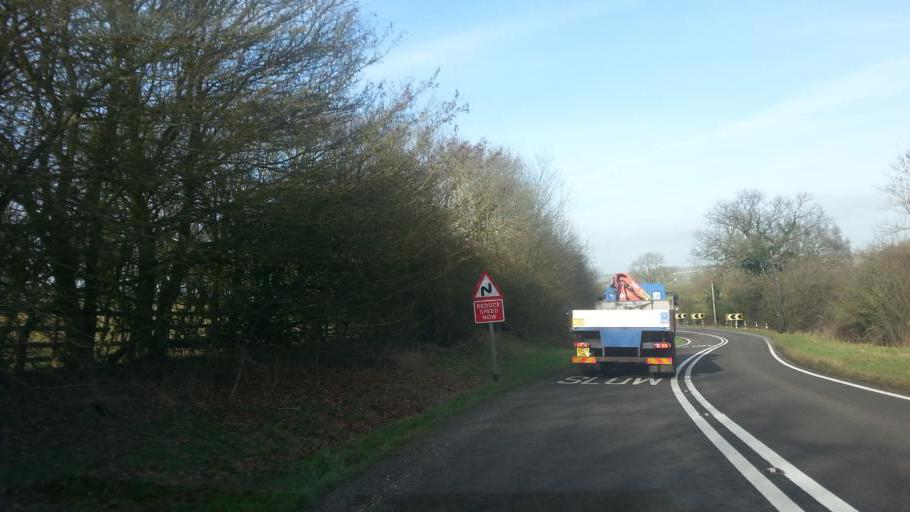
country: GB
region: England
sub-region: Leicestershire
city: Houghton on the Hill
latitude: 52.6528
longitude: -0.9083
